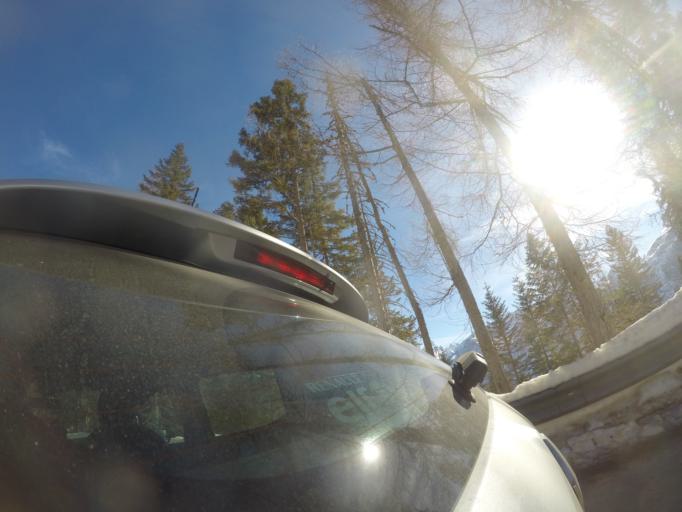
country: IT
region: Veneto
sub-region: Provincia di Belluno
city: Cortina d'Ampezzo
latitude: 46.5588
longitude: 12.2353
